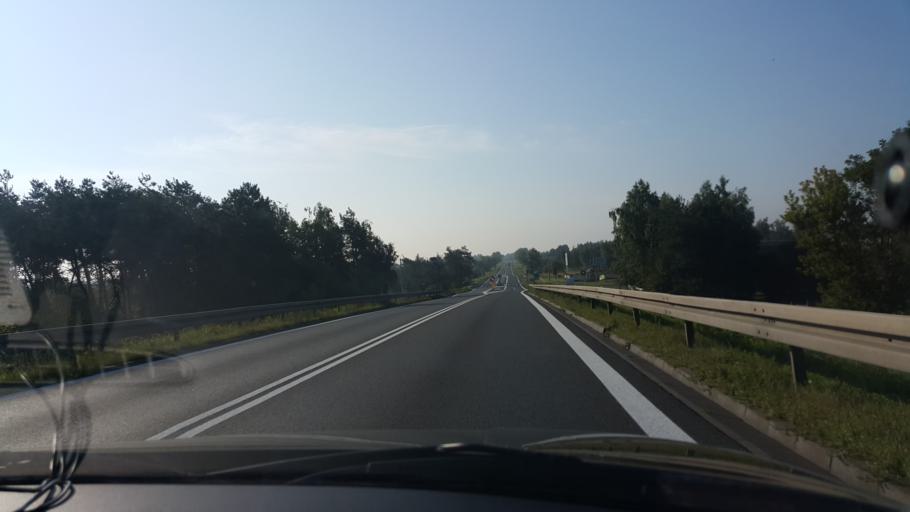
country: PL
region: Masovian Voivodeship
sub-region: Powiat radomski
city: Jastrzebia
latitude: 51.4107
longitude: 21.2389
